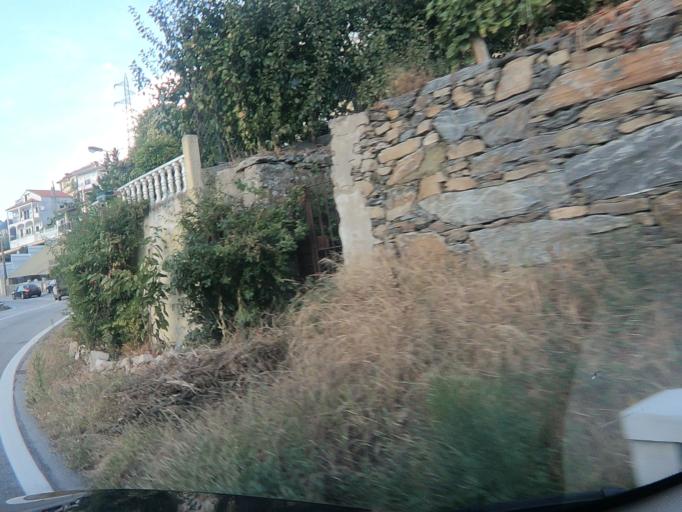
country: PT
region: Vila Real
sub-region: Peso da Regua
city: Peso da Regua
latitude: 41.1846
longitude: -7.7755
